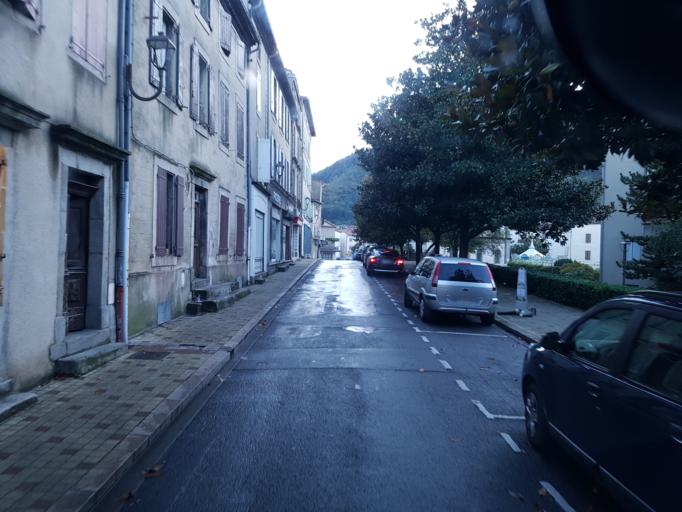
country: FR
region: Midi-Pyrenees
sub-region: Departement du Tarn
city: Mazamet
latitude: 43.4909
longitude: 2.3773
